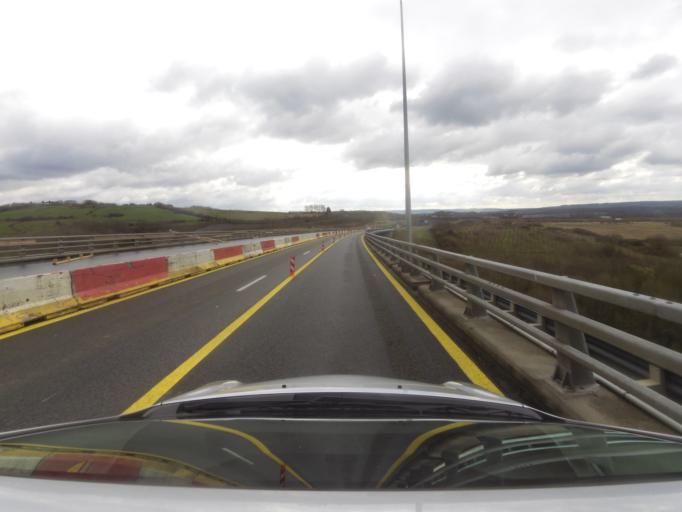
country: FR
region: Nord-Pas-de-Calais
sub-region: Departement du Pas-de-Calais
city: Isques
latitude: 50.6813
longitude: 1.6559
